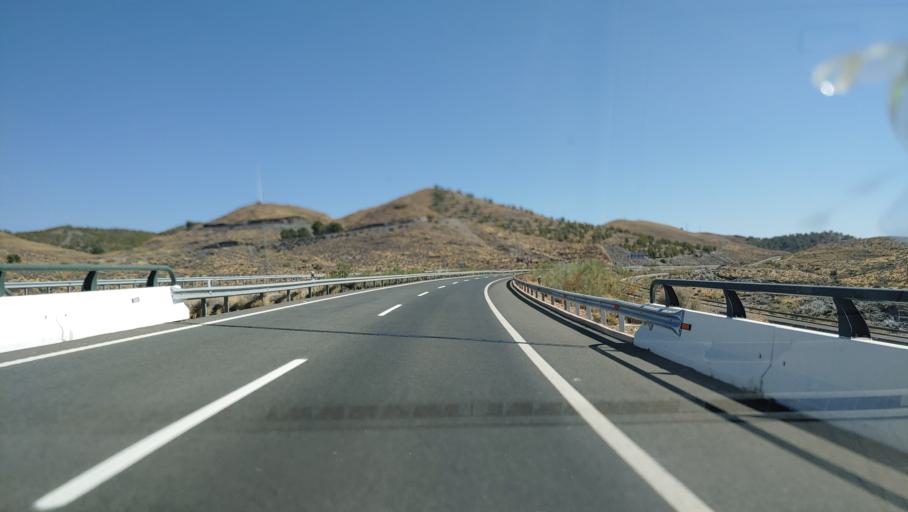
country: ES
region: Andalusia
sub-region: Provincia de Almeria
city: Gergal
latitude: 37.1108
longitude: -2.5295
